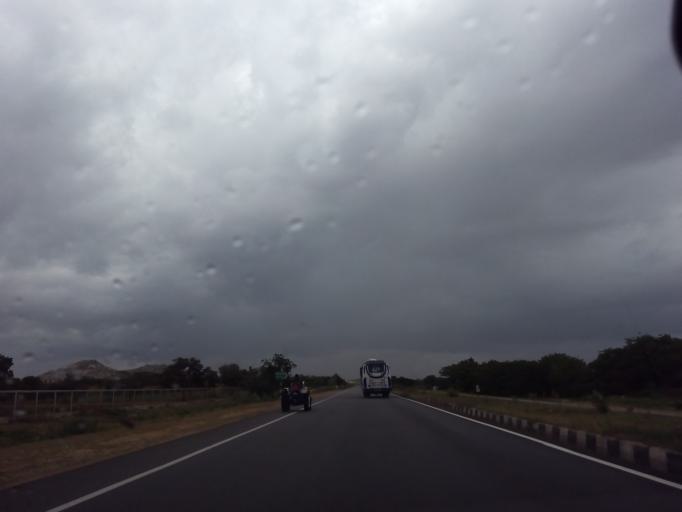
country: IN
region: Karnataka
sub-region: Chitradurga
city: Chitradurga
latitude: 14.2702
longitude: 76.3290
